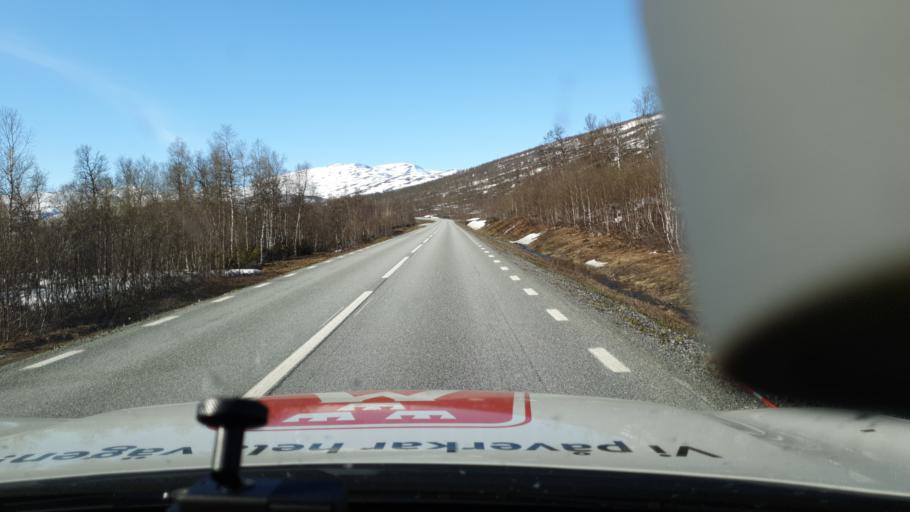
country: NO
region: Nordland
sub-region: Rana
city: Mo i Rana
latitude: 66.0690
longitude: 14.8737
